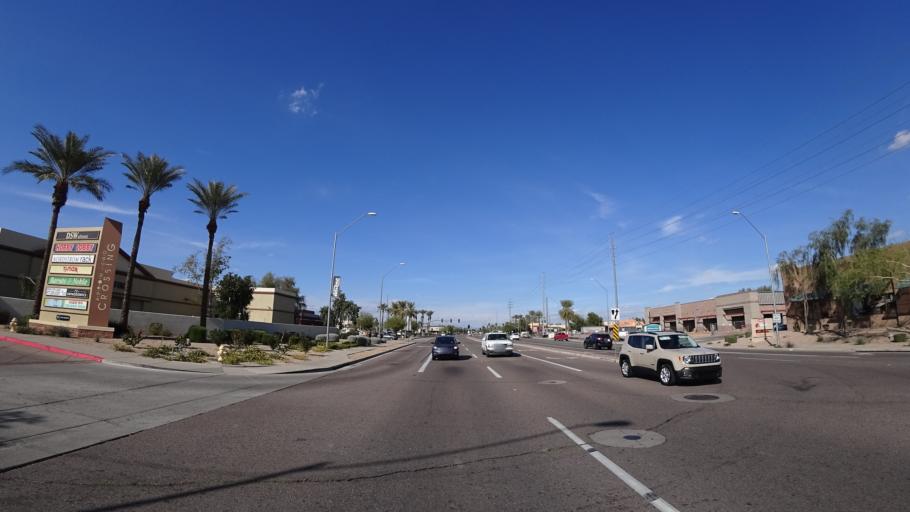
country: US
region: Arizona
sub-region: Maricopa County
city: Peoria
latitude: 33.6368
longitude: -112.2203
